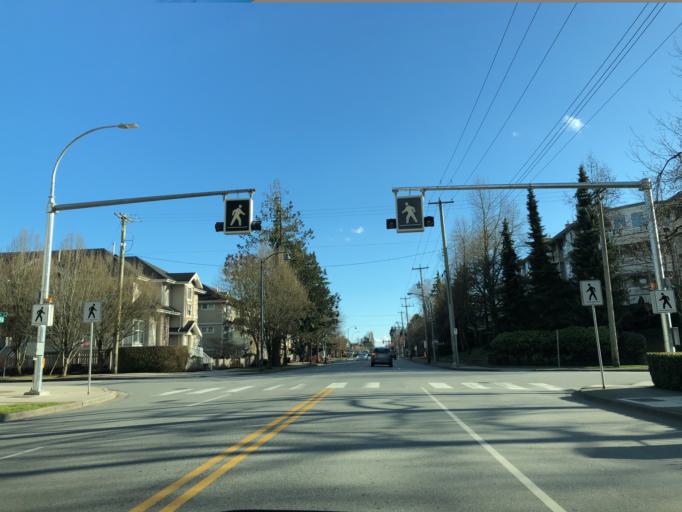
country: CA
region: British Columbia
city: Richmond
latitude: 49.1578
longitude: -123.1254
